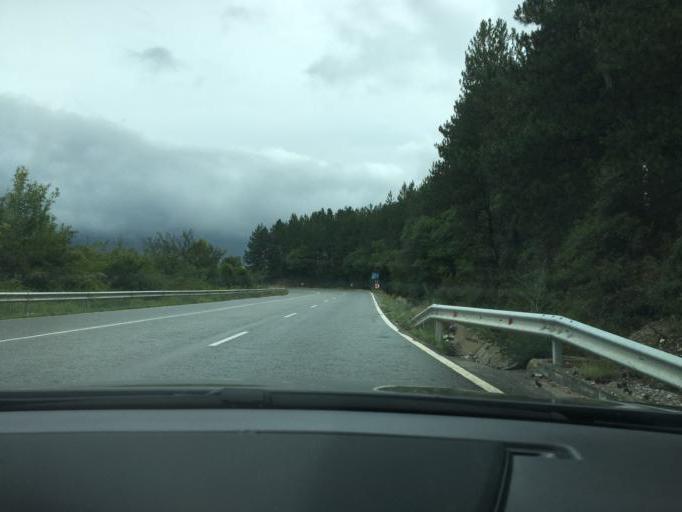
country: BG
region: Kyustendil
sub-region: Obshtina Bobovdol
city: Bobovdol
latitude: 42.2672
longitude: 22.9555
